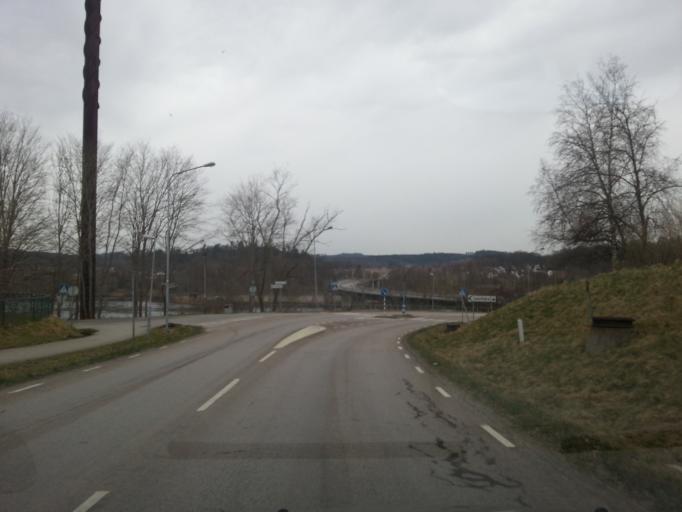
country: SE
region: Vaestra Goetaland
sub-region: Lilla Edets Kommun
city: Lilla Edet
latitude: 58.1334
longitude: 12.1237
